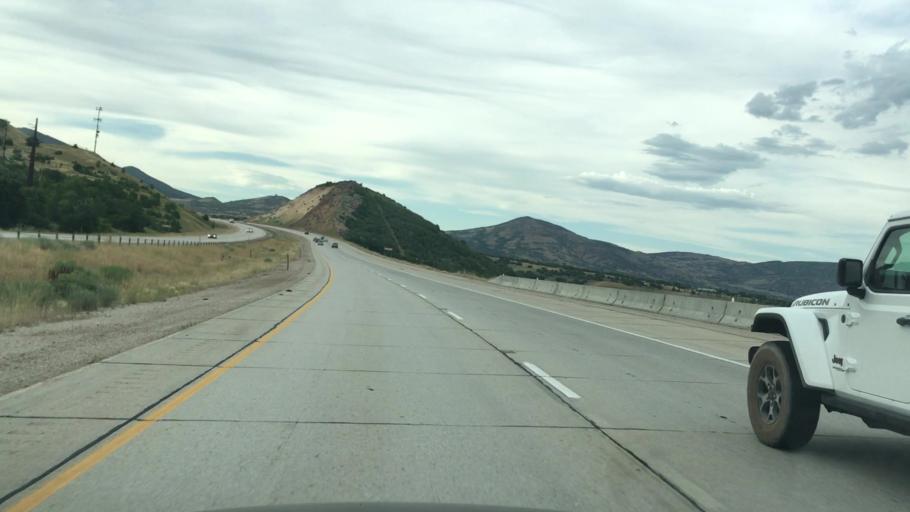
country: US
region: Utah
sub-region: Summit County
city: Park City
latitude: 40.6080
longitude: -111.4289
